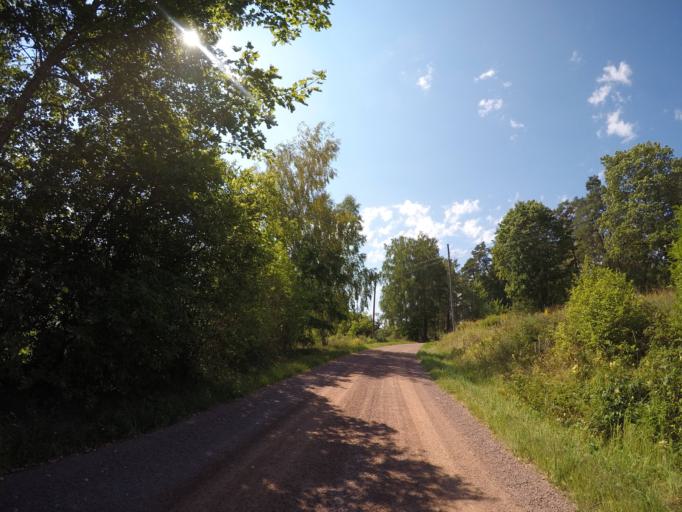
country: AX
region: Alands landsbygd
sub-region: Finstroem
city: Finstroem
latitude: 60.2184
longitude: 19.8600
